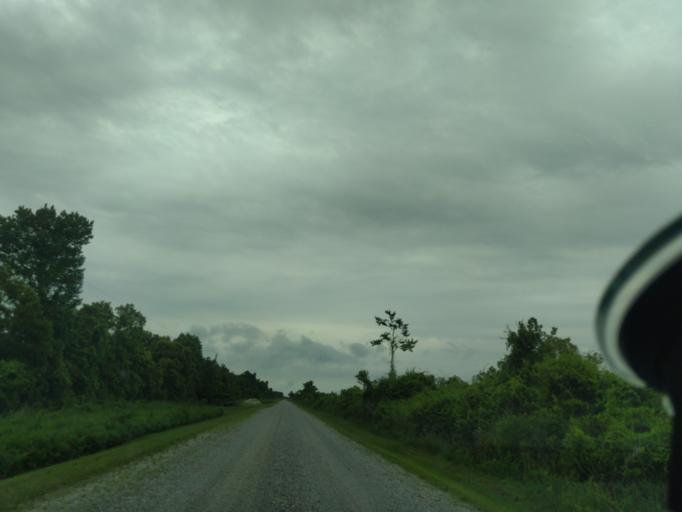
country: US
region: North Carolina
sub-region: Beaufort County
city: Belhaven
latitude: 35.7419
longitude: -76.4816
